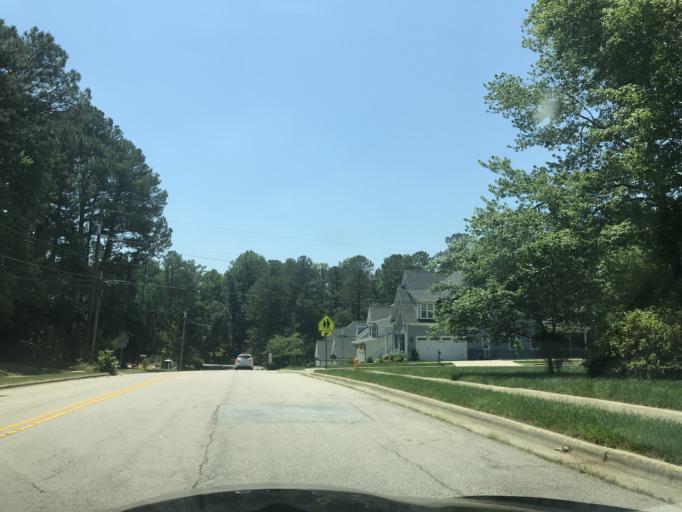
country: US
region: North Carolina
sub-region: Wake County
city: West Raleigh
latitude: 35.8548
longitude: -78.6506
